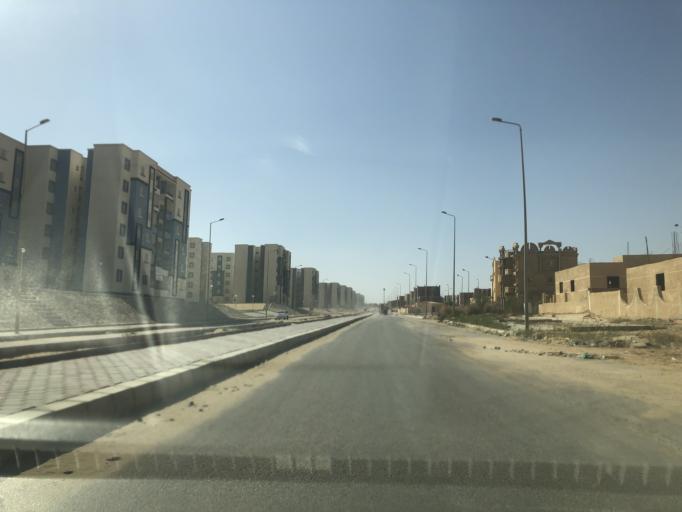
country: EG
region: Al Jizah
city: Madinat Sittah Uktubar
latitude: 29.9300
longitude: 30.9891
